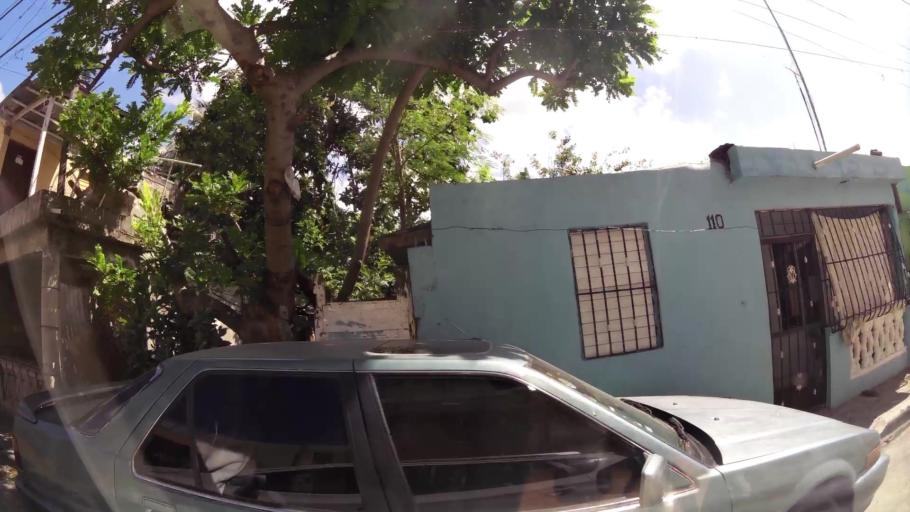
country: DO
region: San Cristobal
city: San Cristobal
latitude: 18.4294
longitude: -70.1157
